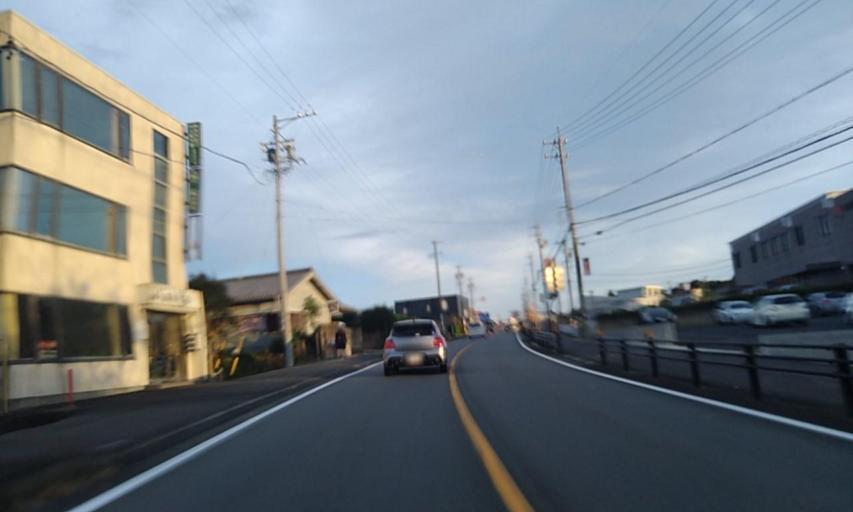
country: JP
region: Mie
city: Toba
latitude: 34.3303
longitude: 136.8366
